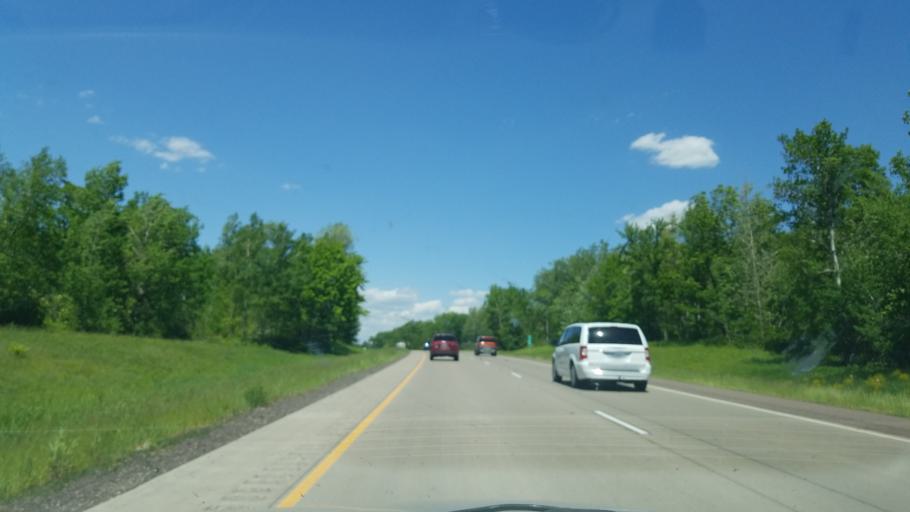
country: US
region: Minnesota
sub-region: Pine County
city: Sandstone
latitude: 46.2244
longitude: -92.8288
